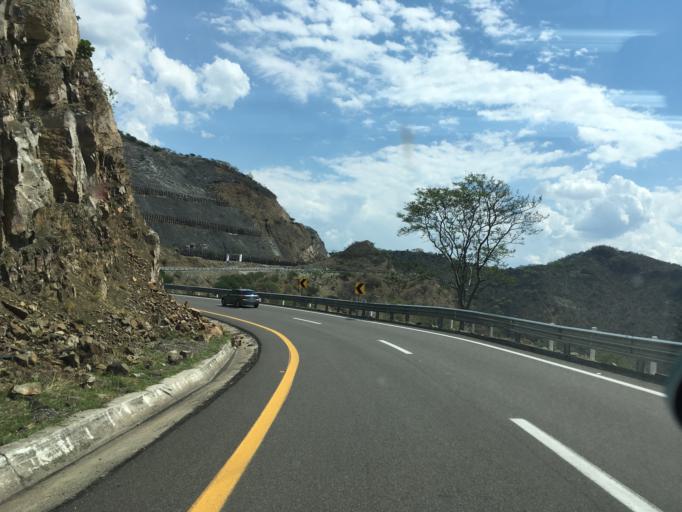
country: MX
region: Puebla
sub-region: San Jose Miahuatlan
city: San Pedro Tetitlan
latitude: 18.1151
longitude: -97.3401
